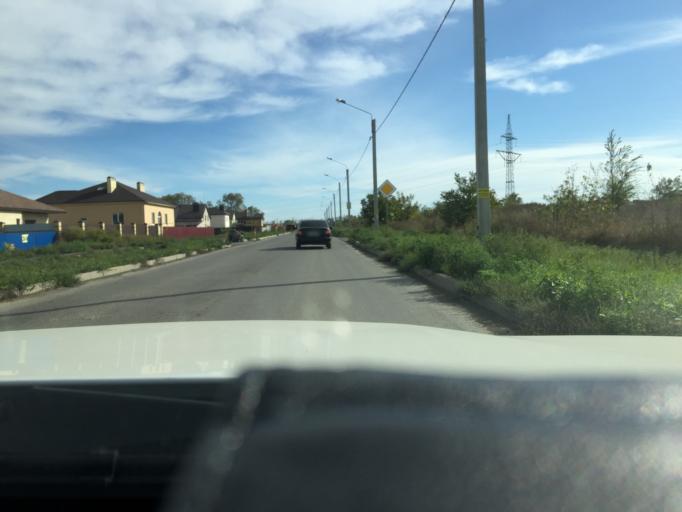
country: RU
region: Rostov
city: Imeni Chkalova
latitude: 47.2981
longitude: 39.8093
